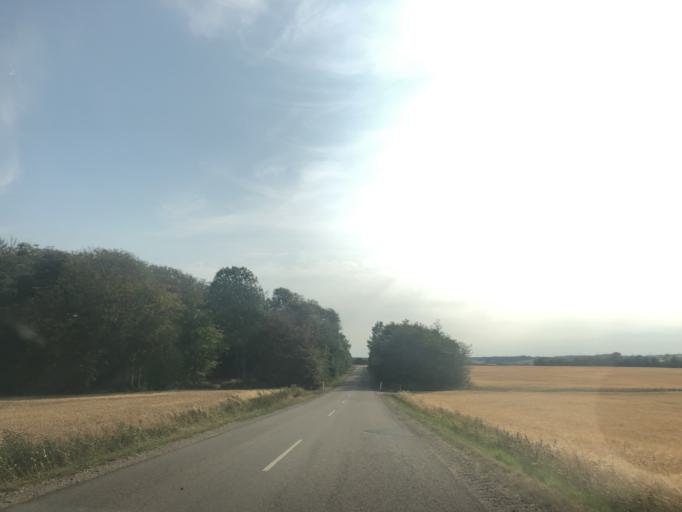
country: DK
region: Central Jutland
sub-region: Skive Kommune
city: Skive
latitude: 56.7481
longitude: 9.0428
